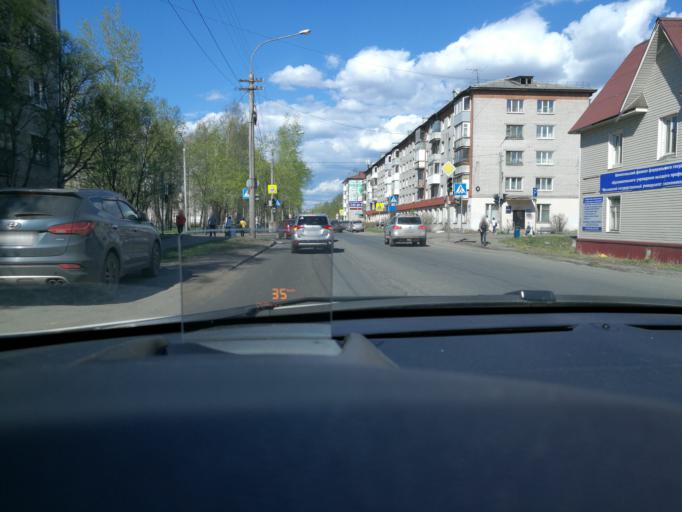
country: RU
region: Arkhangelskaya
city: Arkhangel'sk
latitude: 64.5493
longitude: 40.5353
